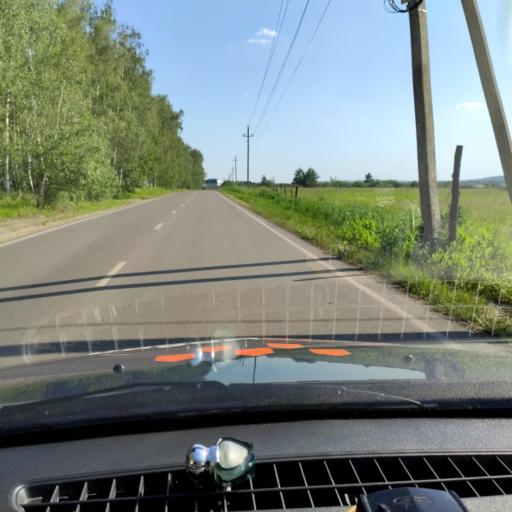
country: RU
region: Voronezj
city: Podgornoye
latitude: 51.8432
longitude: 39.1450
